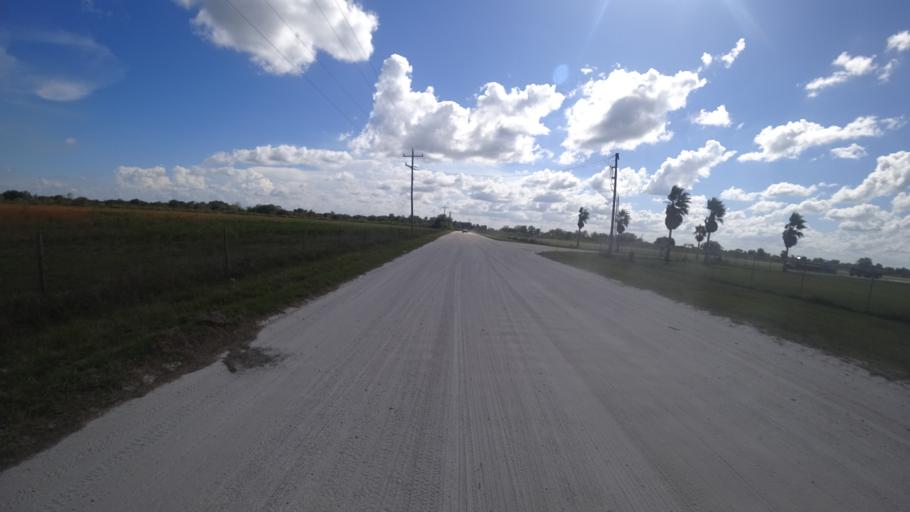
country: US
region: Florida
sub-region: DeSoto County
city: Arcadia
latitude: 27.3133
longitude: -82.1007
